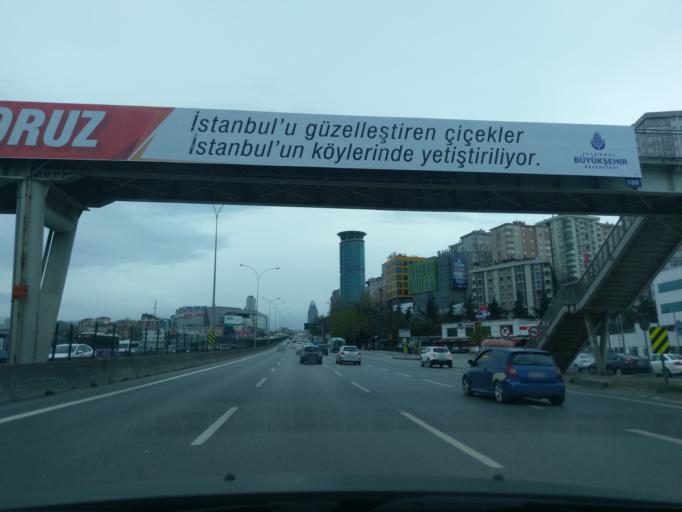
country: TR
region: Istanbul
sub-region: Atasehir
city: Atasehir
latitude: 40.9910
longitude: 29.0774
